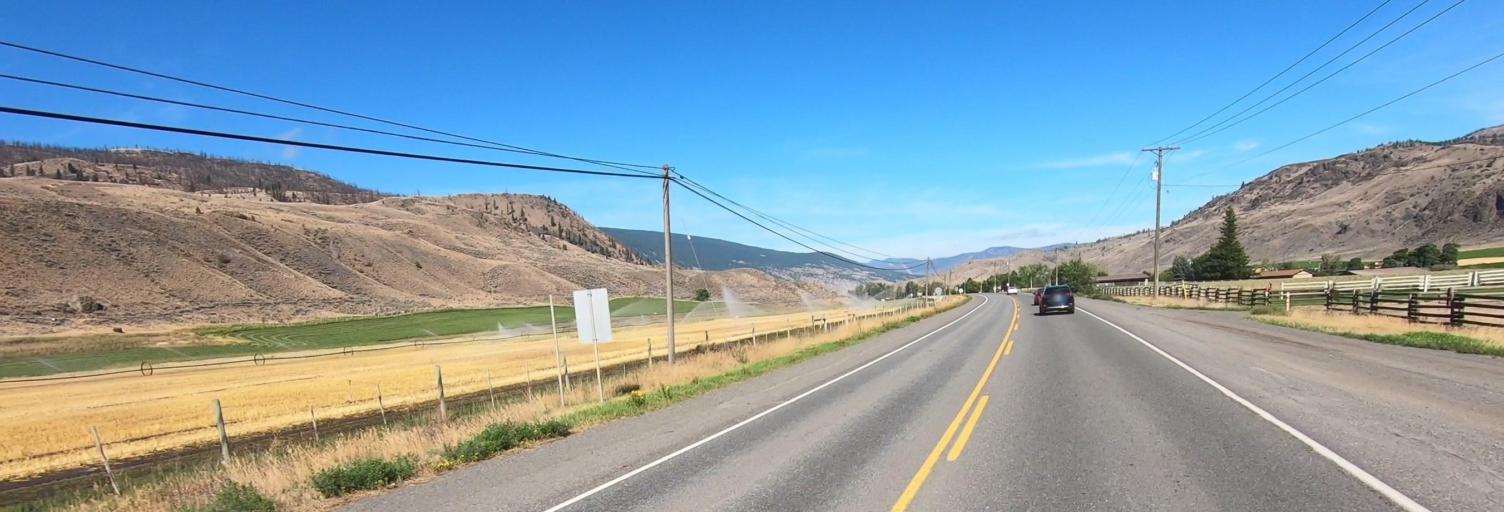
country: CA
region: British Columbia
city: Cache Creek
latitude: 50.8176
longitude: -121.3308
